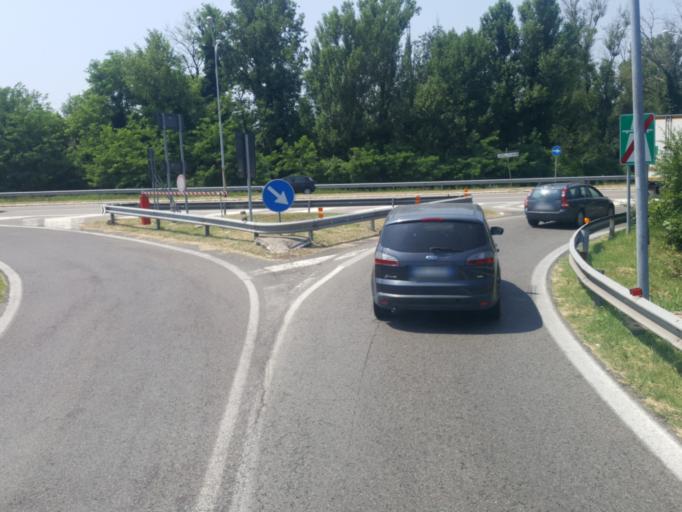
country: IT
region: Emilia-Romagna
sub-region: Provincia di Bologna
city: Calderara di Reno
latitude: 44.5270
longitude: 11.2486
